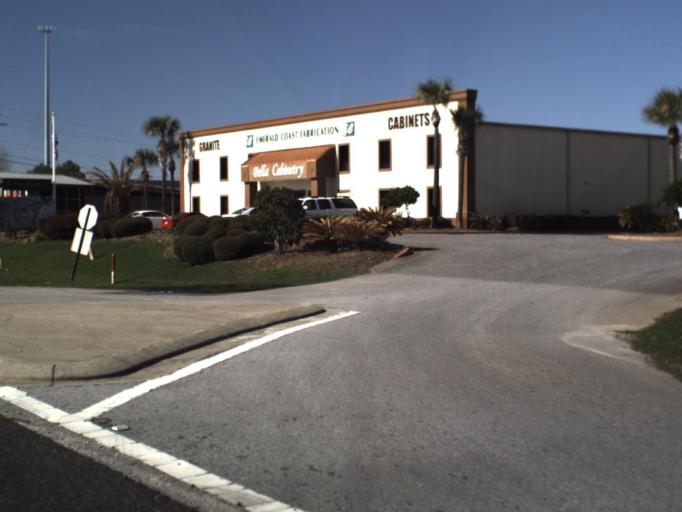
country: US
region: Florida
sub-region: Bay County
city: Laguna Beach
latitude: 30.2376
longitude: -85.9070
